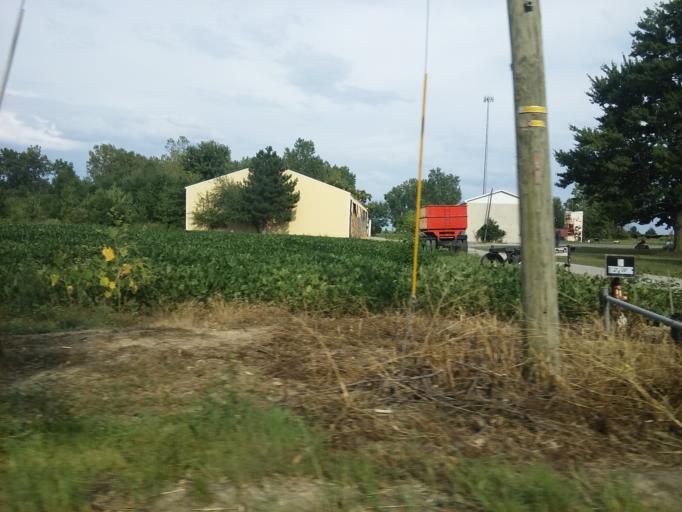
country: US
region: Ohio
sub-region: Hancock County
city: McComb
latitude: 41.1930
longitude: -83.7844
